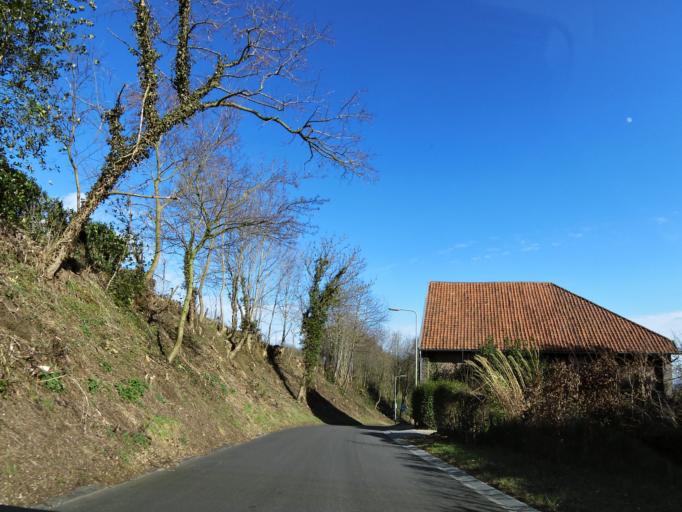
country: NL
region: Limburg
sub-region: Valkenburg aan de Geul
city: Schin op Geul
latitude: 50.8197
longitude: 5.8654
